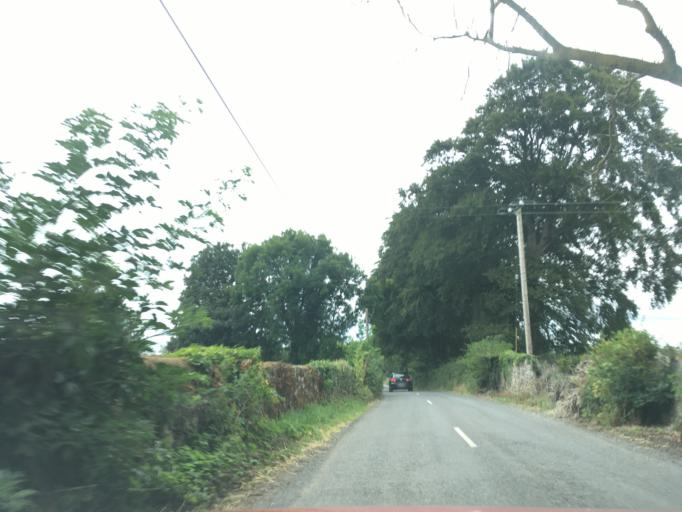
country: IE
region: Munster
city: Cahir
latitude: 52.4597
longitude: -7.9890
